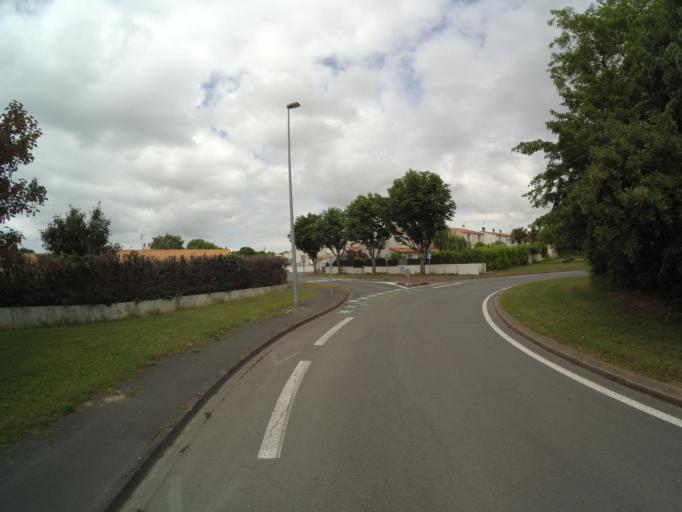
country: FR
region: Poitou-Charentes
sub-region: Departement de la Charente-Maritime
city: Rochefort
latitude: 45.9580
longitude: -0.9696
